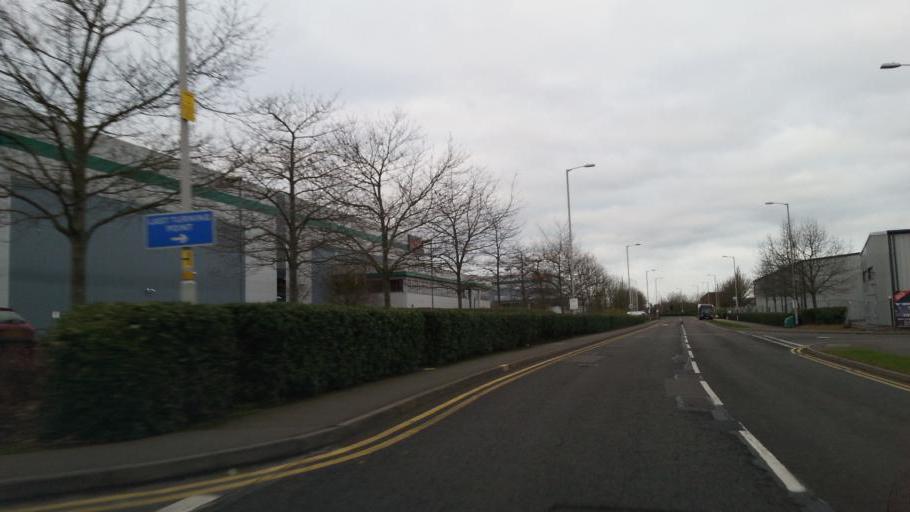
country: GB
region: England
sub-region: Coventry
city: Keresley
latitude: 52.4567
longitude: -1.5244
